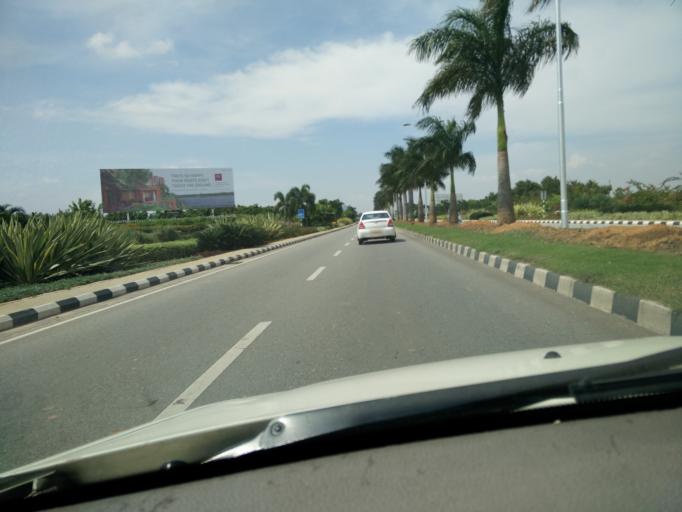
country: IN
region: Karnataka
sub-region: Bangalore Rural
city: Devanhalli
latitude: 13.1980
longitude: 77.6963
